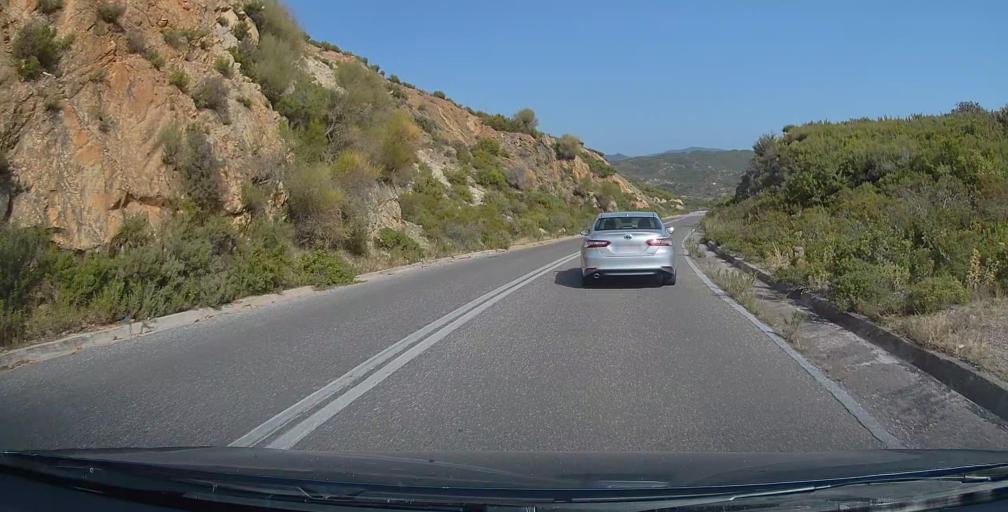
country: GR
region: Central Macedonia
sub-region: Nomos Chalkidikis
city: Sykia
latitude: 39.9869
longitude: 23.9590
